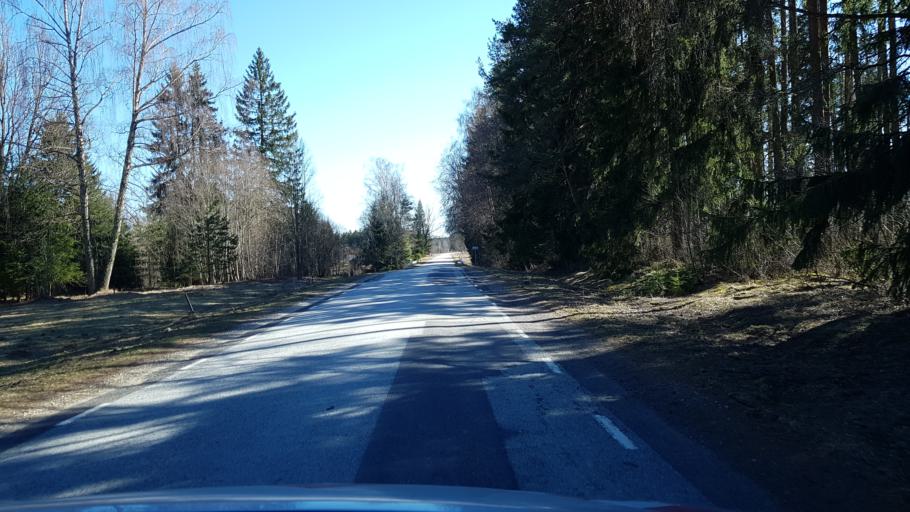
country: EE
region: Laeaene-Virumaa
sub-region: Viru-Nigula vald
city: Kunda
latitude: 59.3812
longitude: 26.5757
